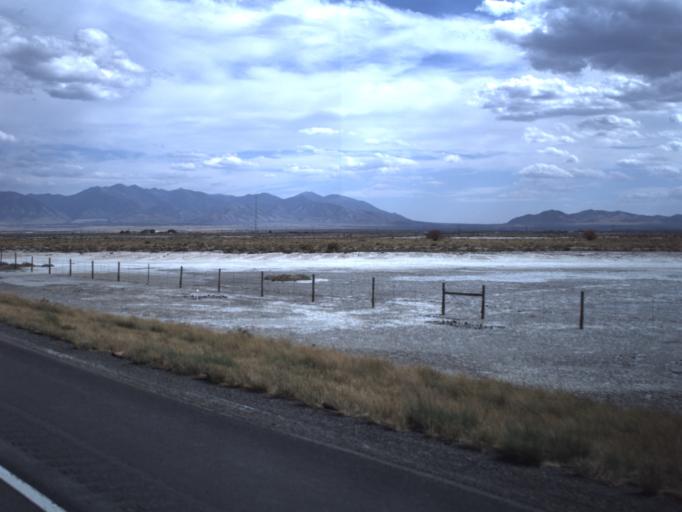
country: US
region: Utah
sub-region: Tooele County
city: Grantsville
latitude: 40.6926
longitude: -112.4678
